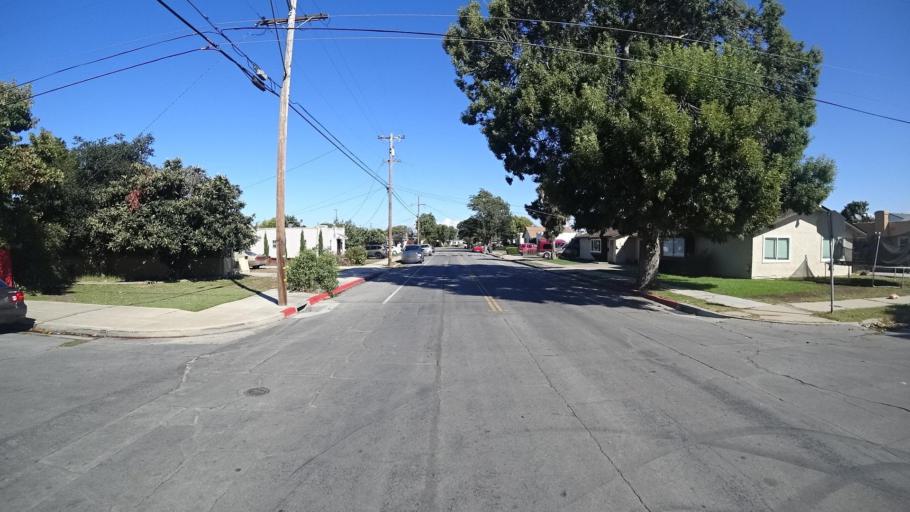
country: US
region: California
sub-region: Monterey County
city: Salinas
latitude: 36.6759
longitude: -121.6696
